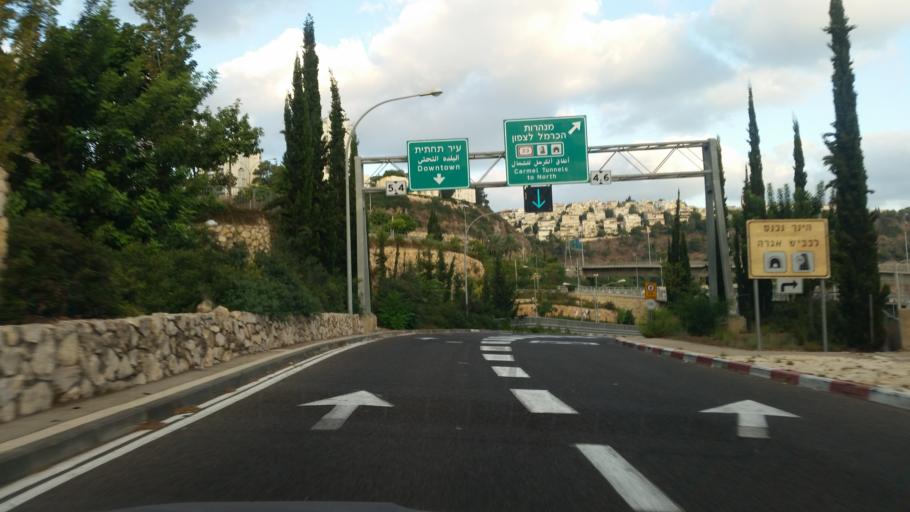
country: IL
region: Haifa
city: Haifa
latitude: 32.7894
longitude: 35.0064
